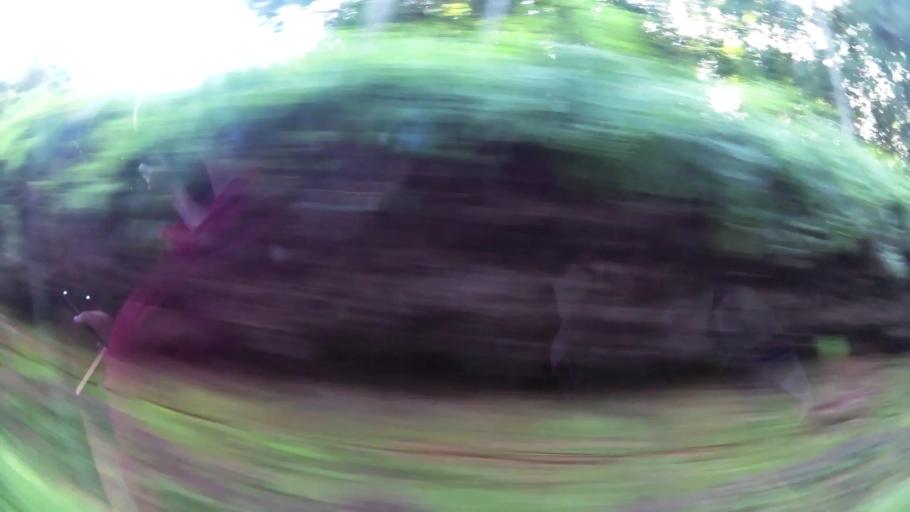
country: GP
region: Guadeloupe
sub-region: Guadeloupe
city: Bouillante
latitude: 16.1752
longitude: -61.6976
